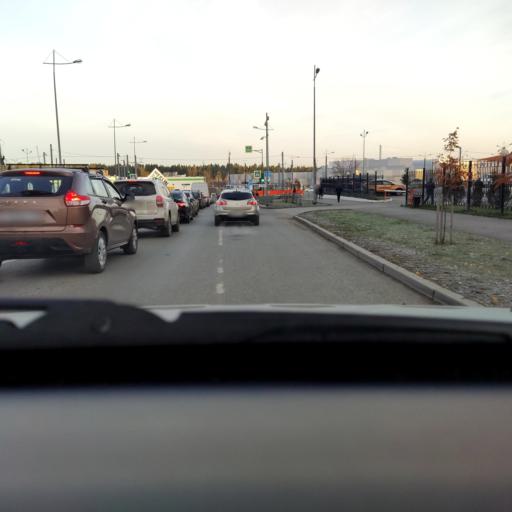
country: RU
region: Perm
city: Kondratovo
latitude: 57.9672
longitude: 56.1512
